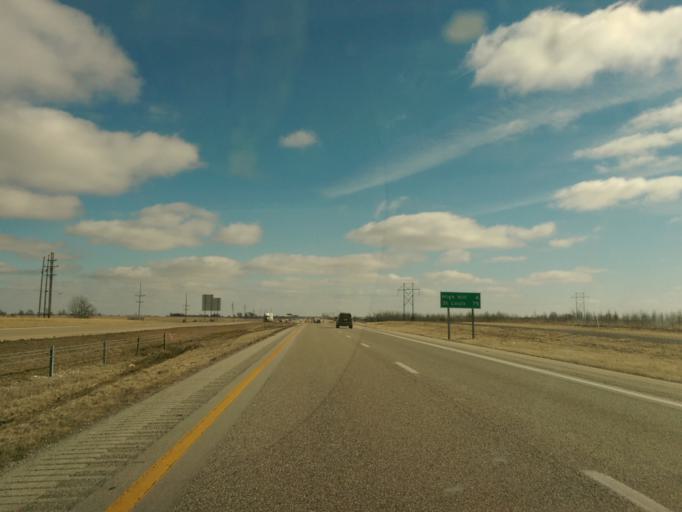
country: US
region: Missouri
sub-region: Montgomery County
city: Montgomery City
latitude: 38.8939
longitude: -91.4365
